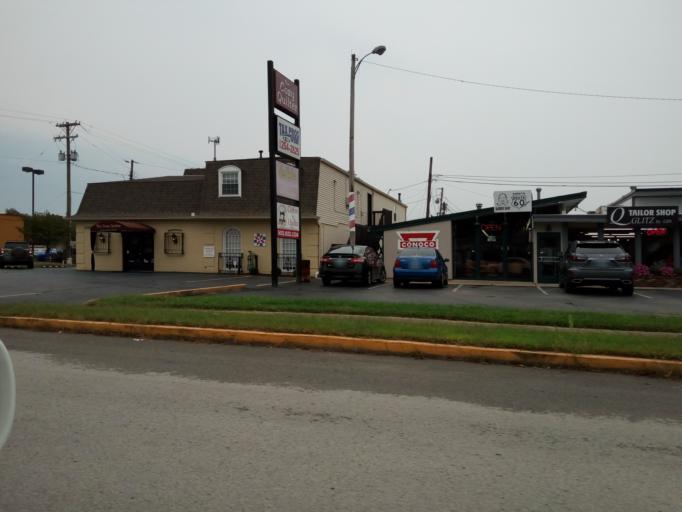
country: US
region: Kentucky
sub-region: Jefferson County
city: Middletown
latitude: 38.2476
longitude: -85.5289
